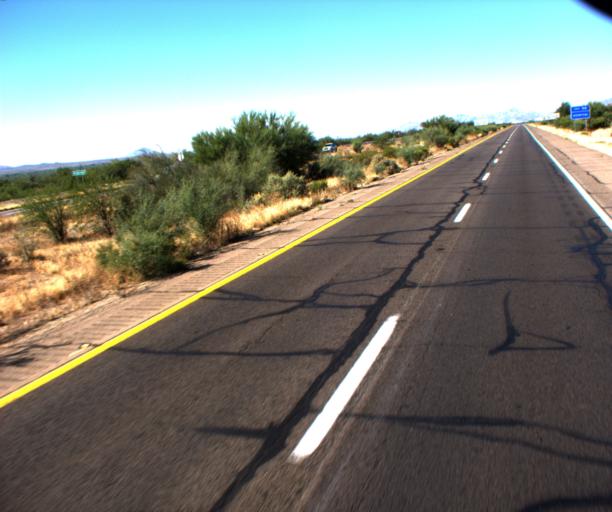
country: US
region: Arizona
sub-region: Pima County
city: Green Valley
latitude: 31.7985
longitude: -111.0173
